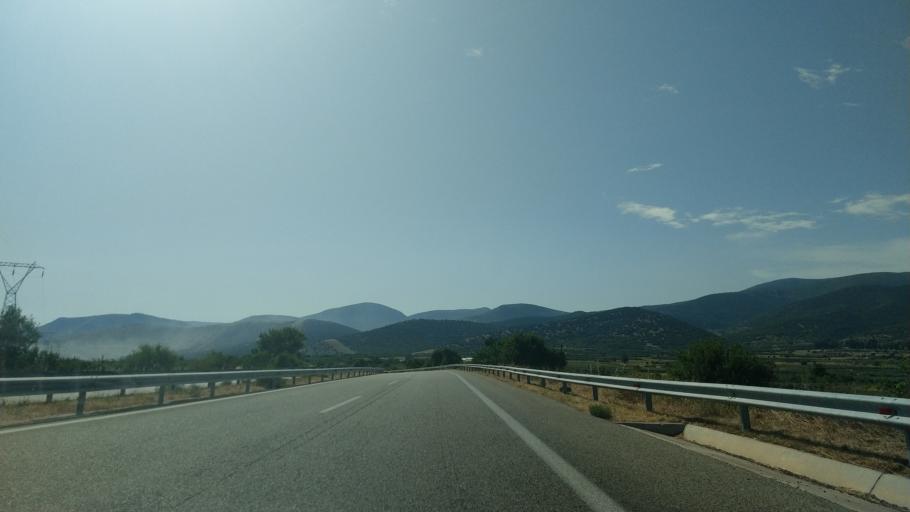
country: GR
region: East Macedonia and Thrace
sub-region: Nomos Kavalas
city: Nea Karvali
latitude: 40.9684
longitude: 24.5165
